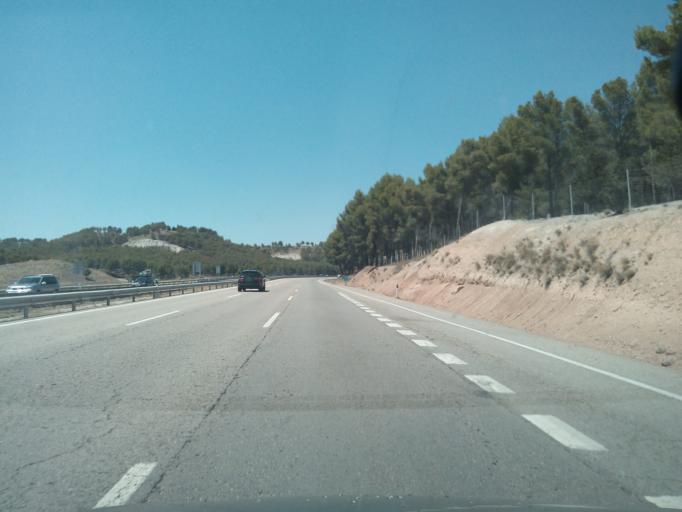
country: ES
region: Castille-La Mancha
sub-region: Province of Toledo
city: Dosbarrios
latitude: 39.8214
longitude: -3.4824
